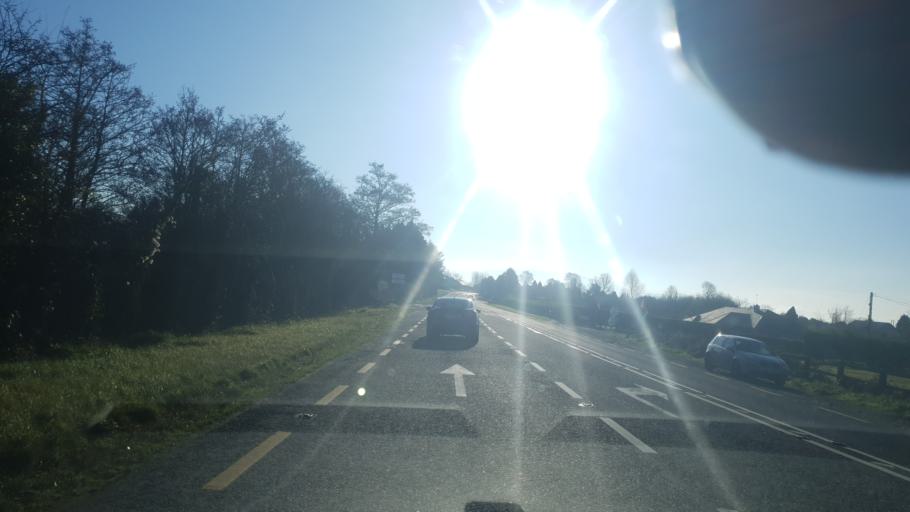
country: IE
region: Munster
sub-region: Ciarrai
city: Cill Airne
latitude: 52.1138
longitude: -9.5167
